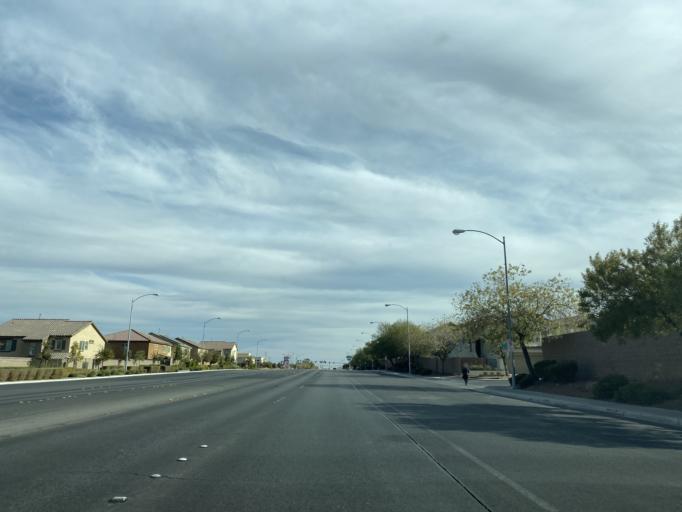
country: US
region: Nevada
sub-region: Clark County
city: Summerlin South
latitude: 36.0701
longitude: -115.3025
